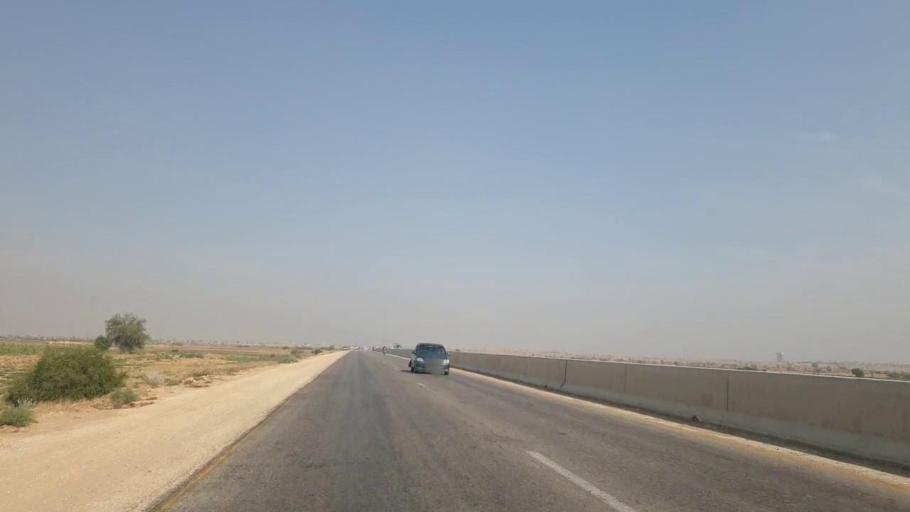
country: PK
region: Sindh
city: Jamshoro
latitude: 25.5567
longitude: 68.3024
